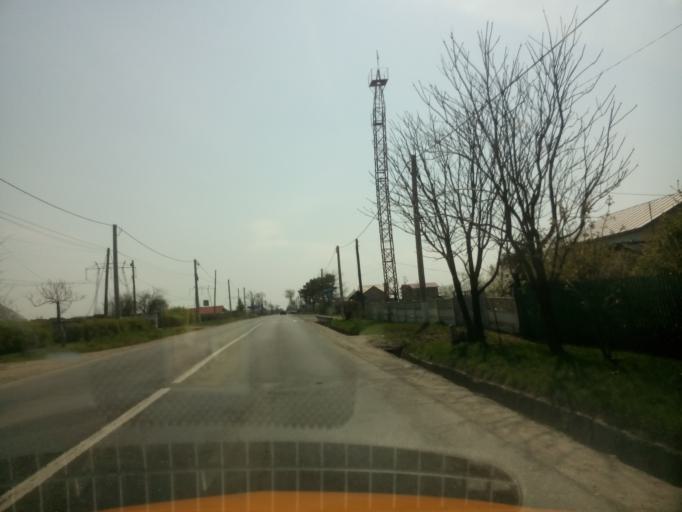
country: RO
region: Calarasi
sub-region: Comuna Frumusani
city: Frumusani
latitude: 44.3164
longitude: 26.2773
